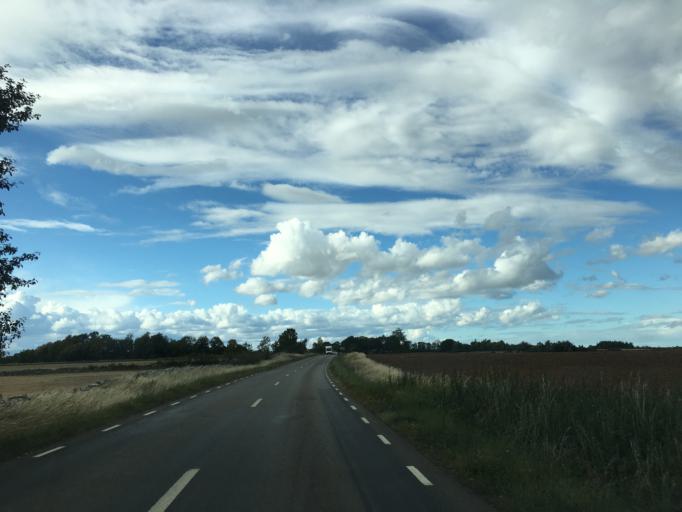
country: SE
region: Kalmar
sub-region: Morbylanga Kommun
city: Moerbylanga
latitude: 56.4095
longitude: 16.4356
